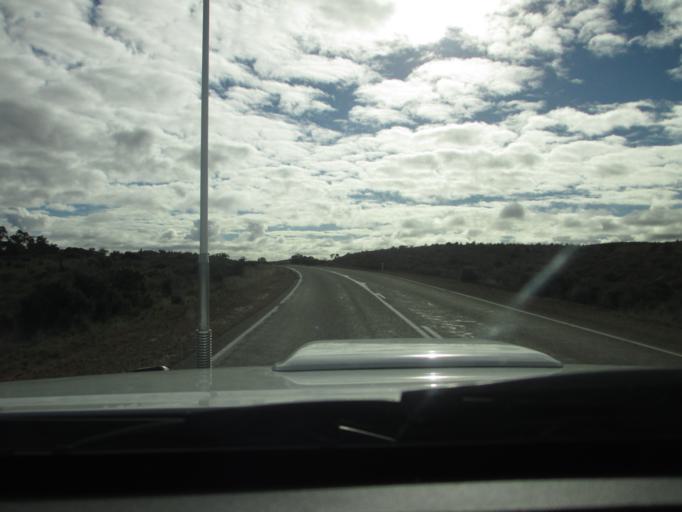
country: AU
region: South Australia
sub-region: Flinders Ranges
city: Quorn
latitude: -32.3159
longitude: 138.4842
